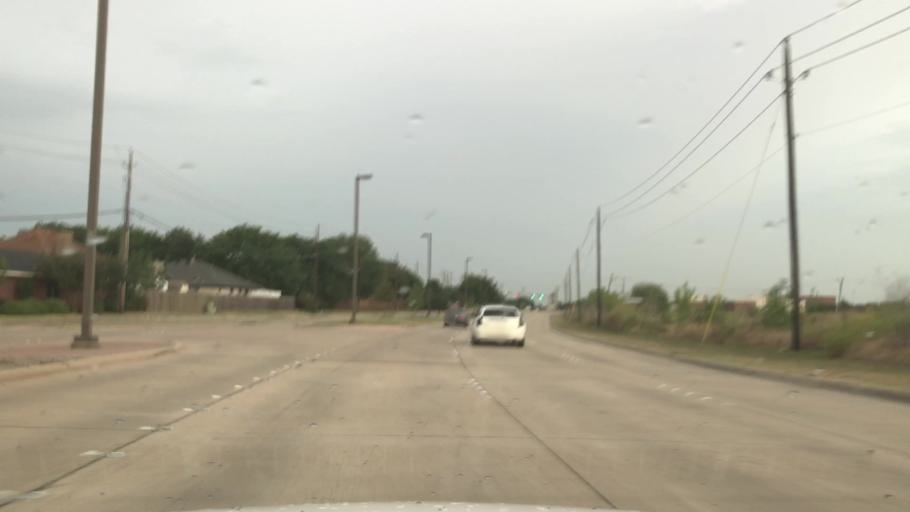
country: US
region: Texas
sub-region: Dallas County
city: Mesquite
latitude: 32.7370
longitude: -96.5617
